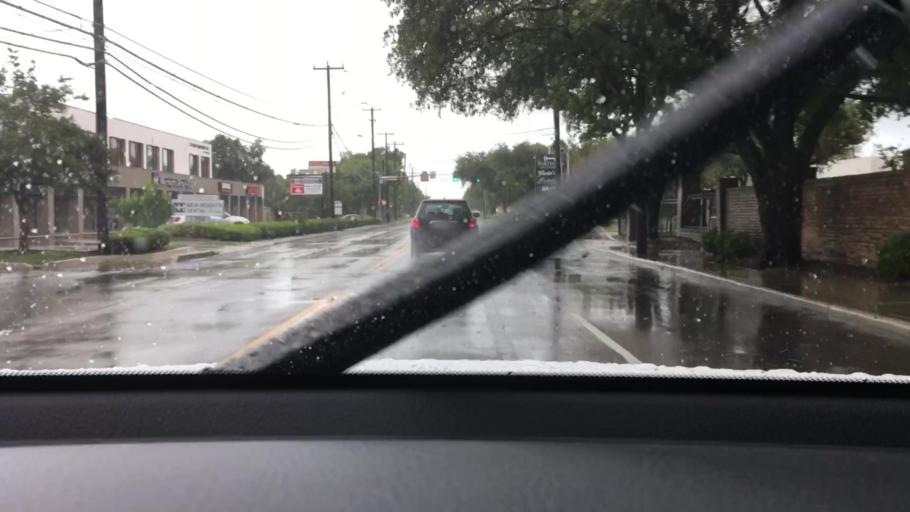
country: US
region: Texas
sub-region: Bexar County
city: Alamo Heights
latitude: 29.5006
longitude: -98.4666
